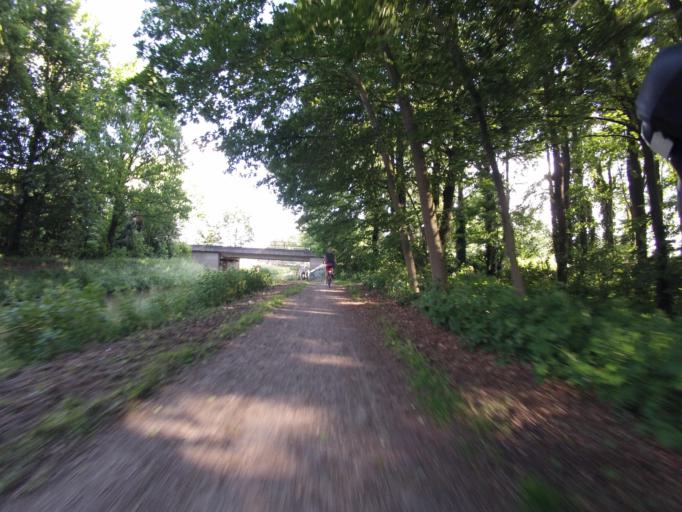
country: DE
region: North Rhine-Westphalia
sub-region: Regierungsbezirk Munster
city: Horstel
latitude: 52.2966
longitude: 7.5968
